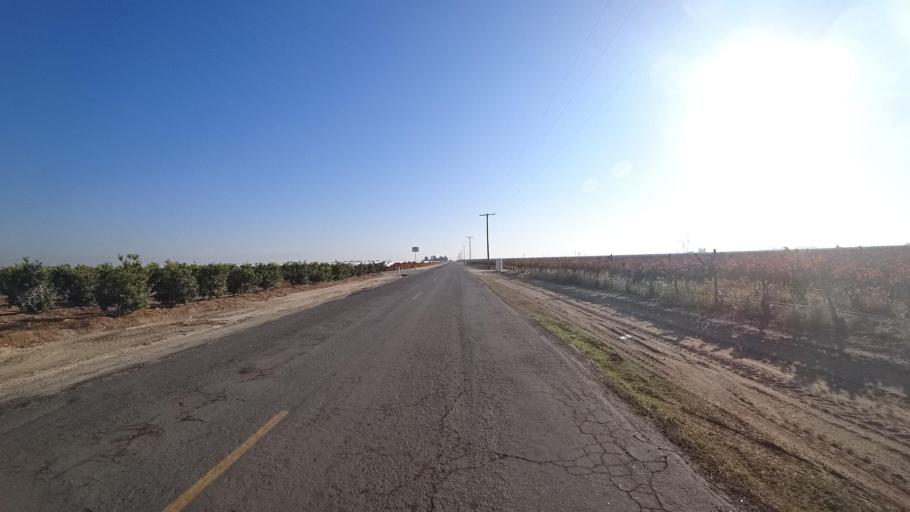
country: US
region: California
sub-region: Kern County
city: Delano
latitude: 35.7686
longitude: -119.2016
